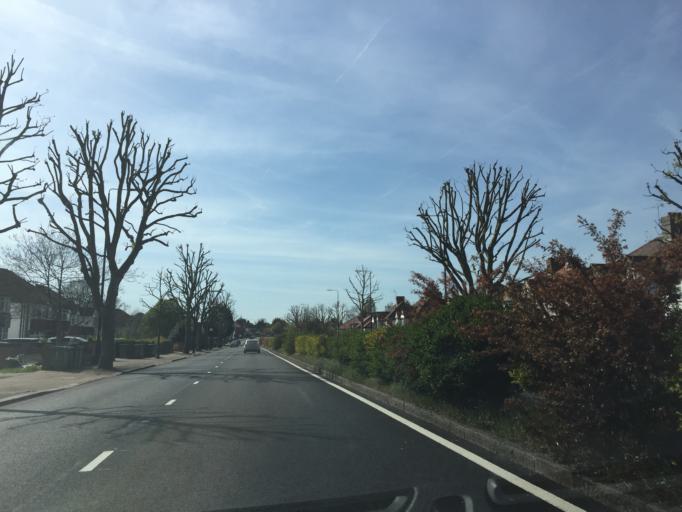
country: GB
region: England
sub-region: Greater London
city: Chislehurst
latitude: 51.4373
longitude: 0.0568
